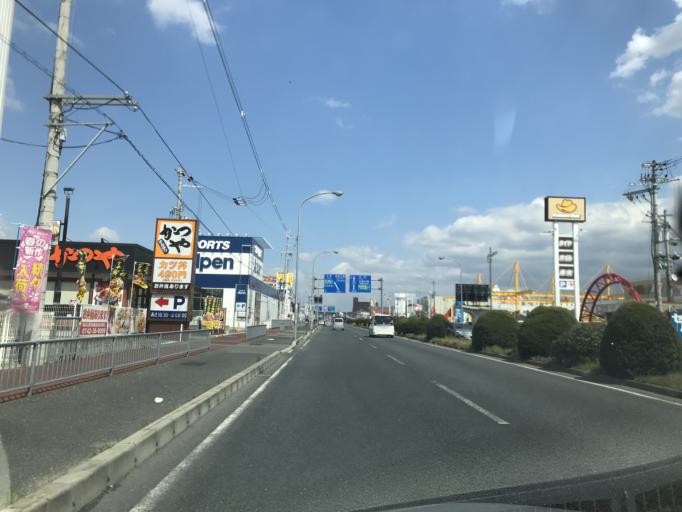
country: JP
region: Nara
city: Nara-shi
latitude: 34.6767
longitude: 135.8004
